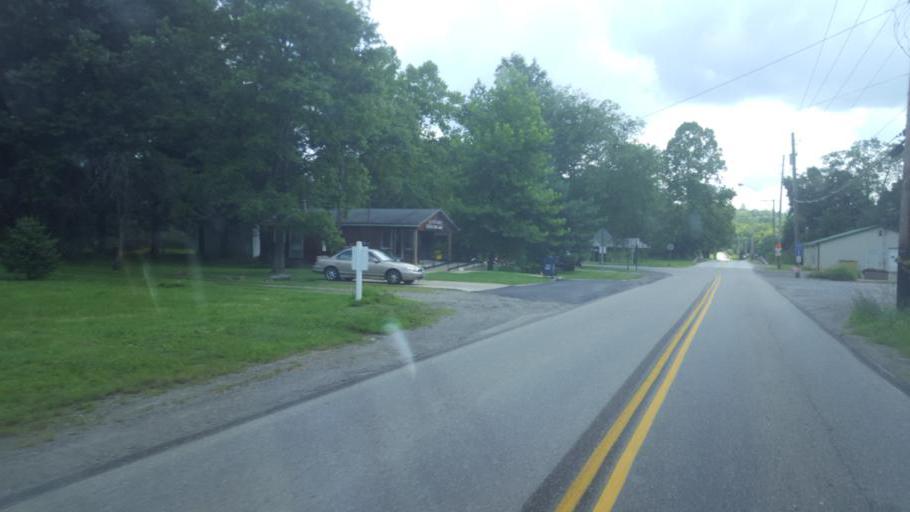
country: US
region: Ohio
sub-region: Columbiana County
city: Lisbon
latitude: 40.7626
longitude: -80.6999
